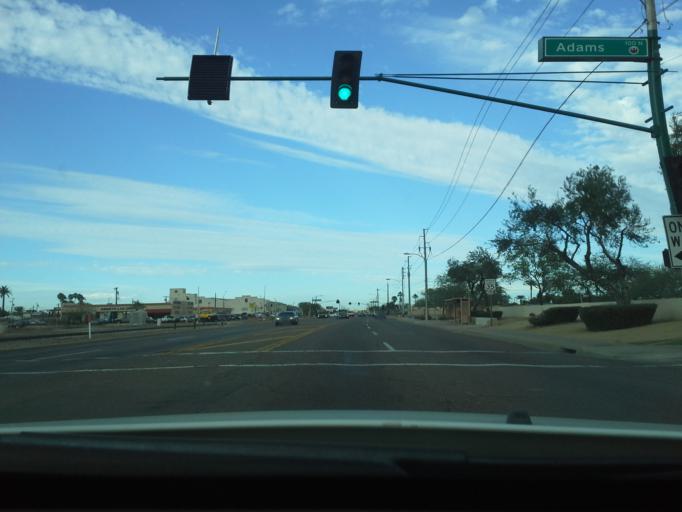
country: US
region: Arizona
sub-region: Maricopa County
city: Phoenix
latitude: 33.4492
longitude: -112.1001
